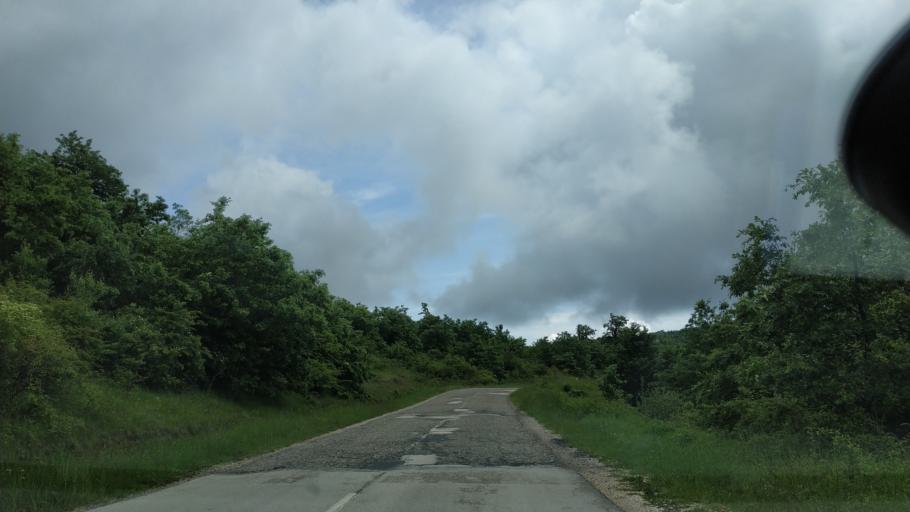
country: RS
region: Central Serbia
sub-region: Zajecarski Okrug
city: Soko Banja
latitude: 43.7172
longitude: 21.9421
